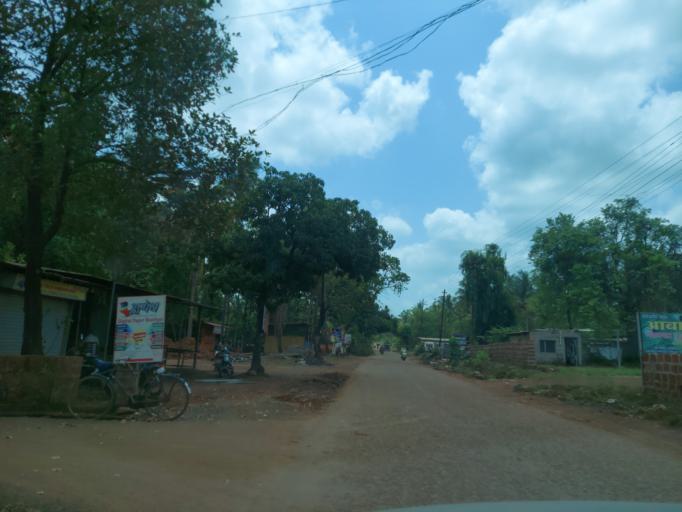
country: IN
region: Maharashtra
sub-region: Sindhudurg
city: Savantvadi
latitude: 15.8203
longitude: 73.8700
